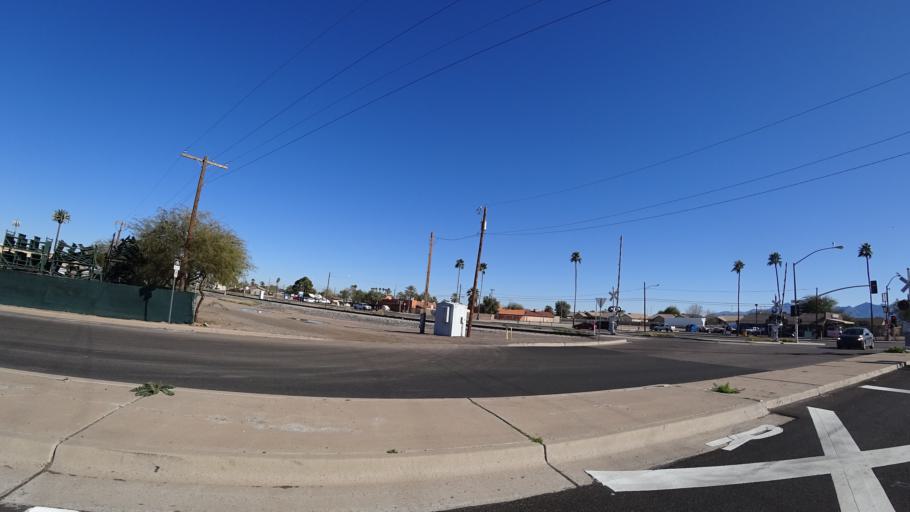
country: US
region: Arizona
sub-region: Maricopa County
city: Goodyear
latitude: 33.4255
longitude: -112.3580
